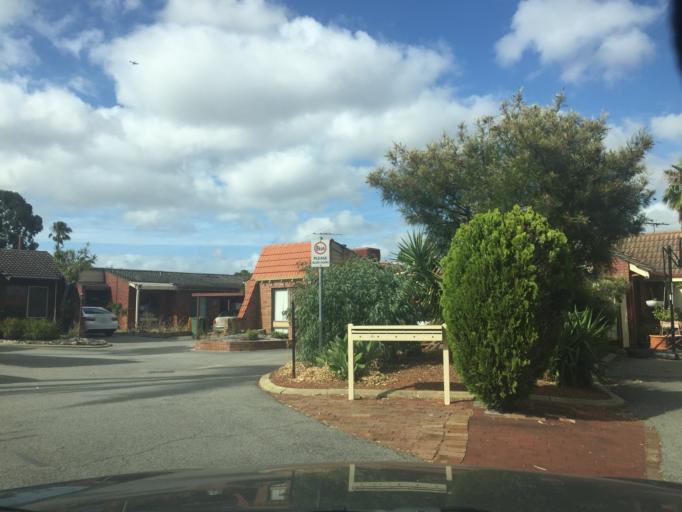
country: AU
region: Western Australia
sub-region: Canning
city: Ferndale
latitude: -32.0436
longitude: 115.9117
